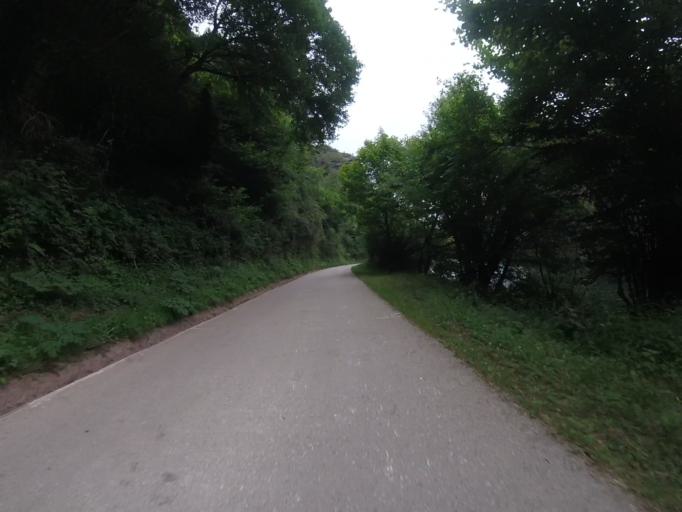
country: ES
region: Navarre
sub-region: Provincia de Navarra
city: Doneztebe
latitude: 43.1396
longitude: -1.6663
